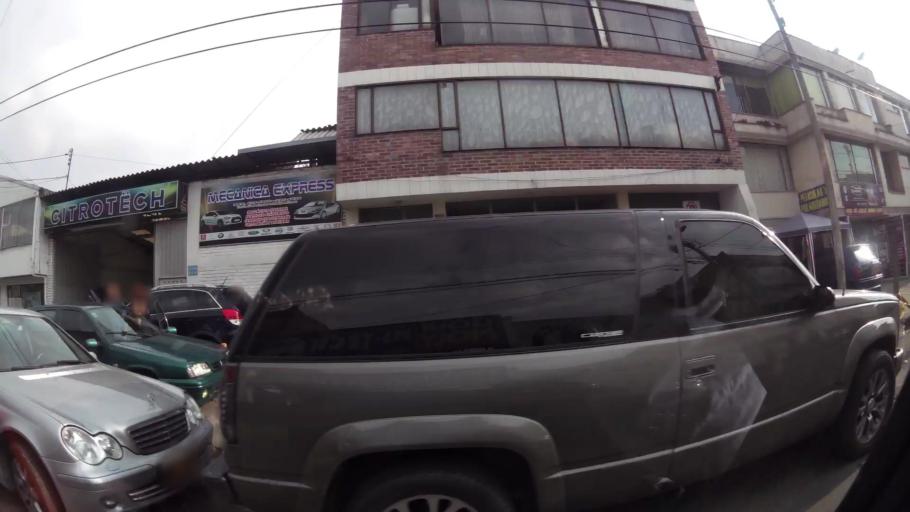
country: CO
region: Bogota D.C.
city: Barrio San Luis
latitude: 4.7200
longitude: -74.0550
